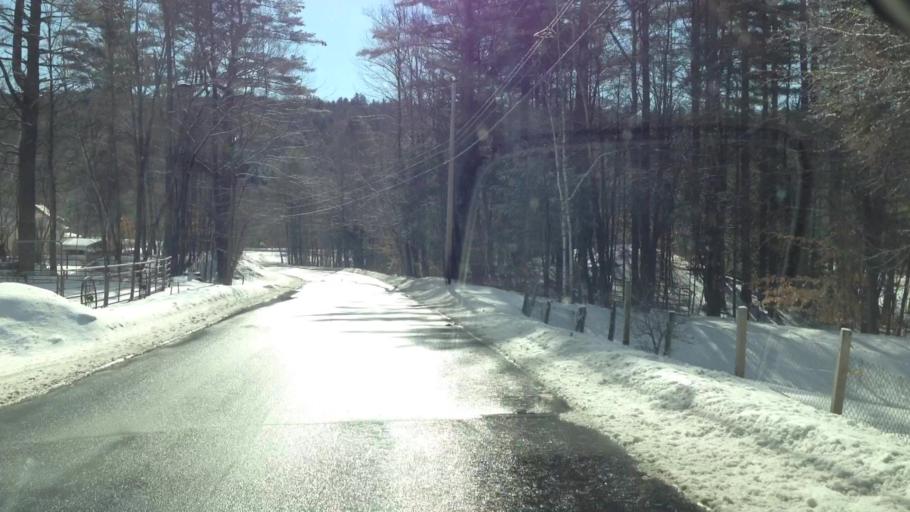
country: US
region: New Hampshire
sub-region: Grafton County
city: Haverhill
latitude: 44.0308
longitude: -72.0153
